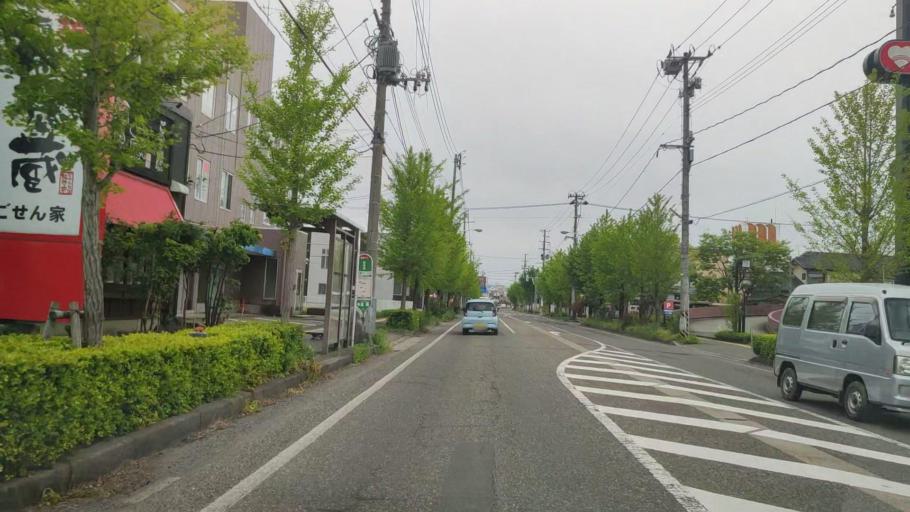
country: JP
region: Niigata
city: Gosen
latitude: 37.7403
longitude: 139.1808
